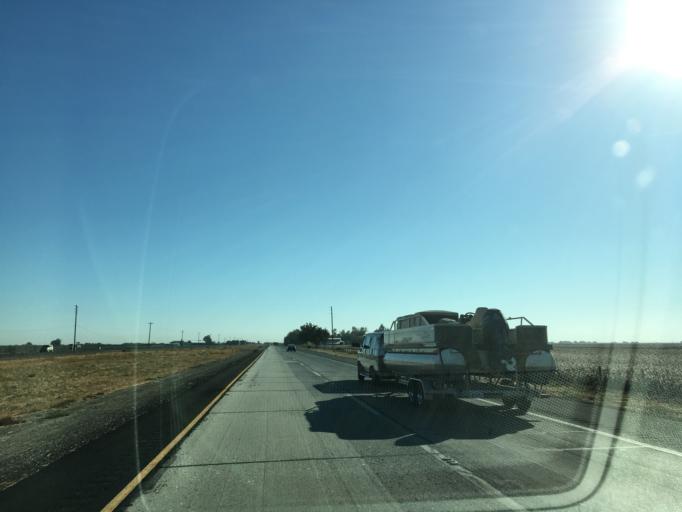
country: US
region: California
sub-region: Merced County
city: Dos Palos
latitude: 37.0509
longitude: -120.5748
